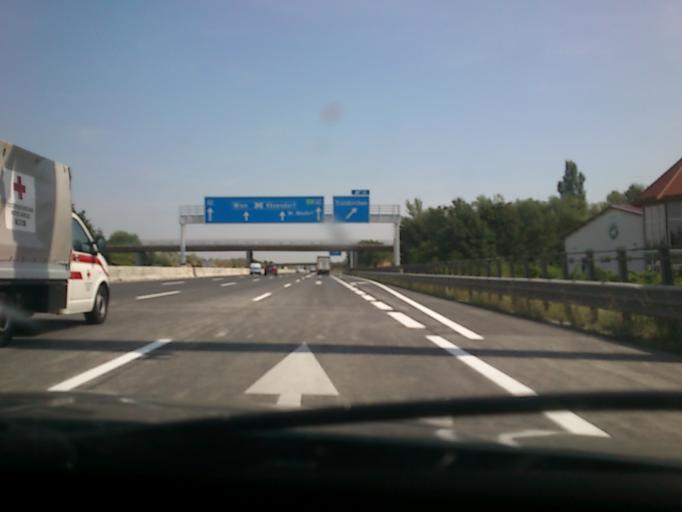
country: AT
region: Lower Austria
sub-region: Politischer Bezirk Baden
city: Traiskirchen
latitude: 47.9974
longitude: 16.2954
